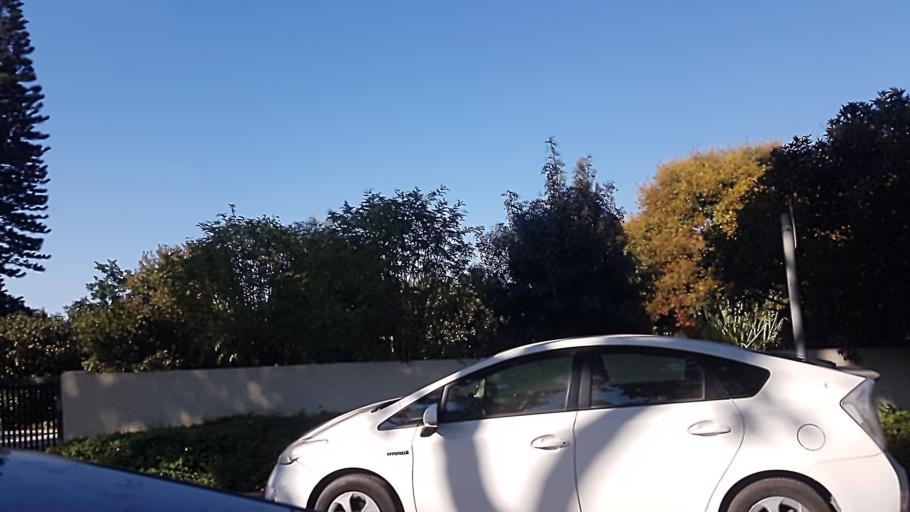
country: IL
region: Central District
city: Kfar Saba
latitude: 32.2098
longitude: 34.9029
